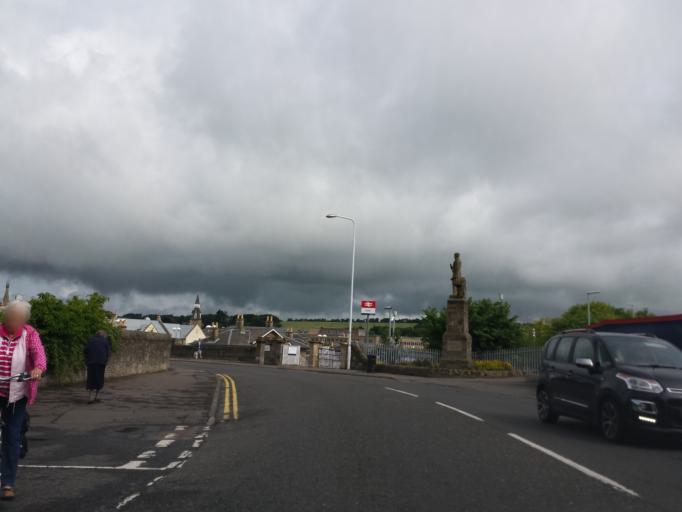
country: GB
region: Scotland
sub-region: Fife
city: Cupar
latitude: 56.3164
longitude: -3.0089
